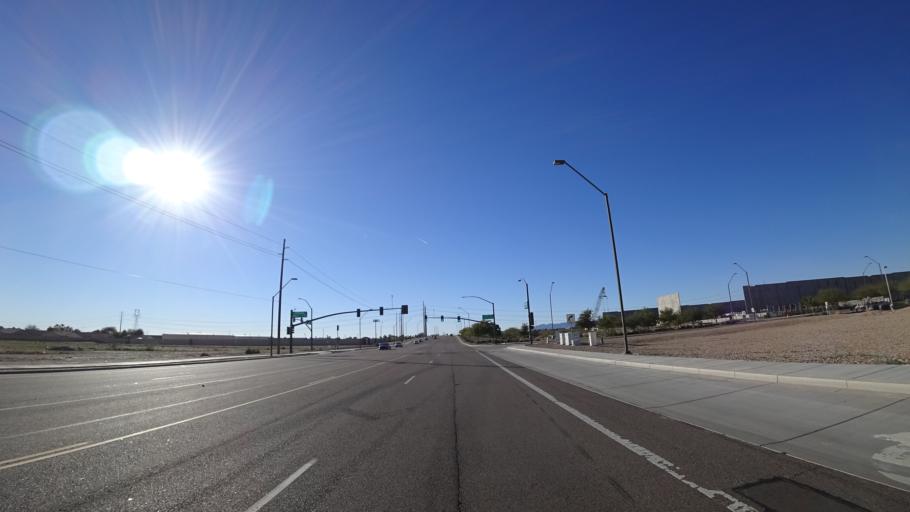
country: US
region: Arizona
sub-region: Maricopa County
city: Avondale
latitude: 33.4496
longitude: -112.3273
